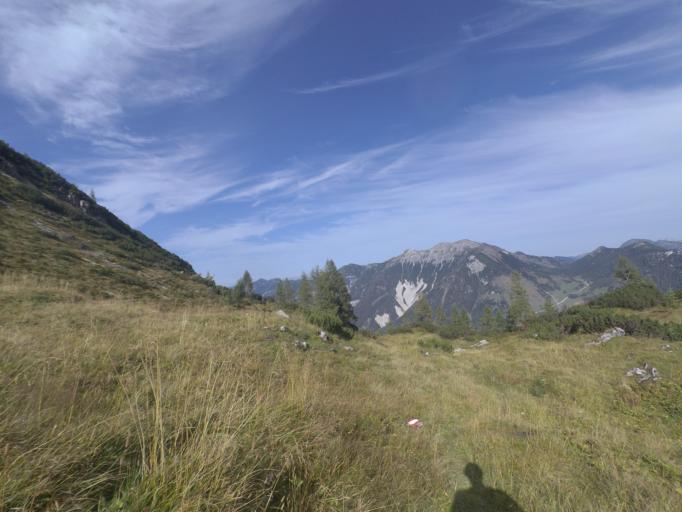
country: AT
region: Salzburg
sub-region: Politischer Bezirk Sankt Johann im Pongau
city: Kleinarl
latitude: 47.2362
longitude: 13.4073
